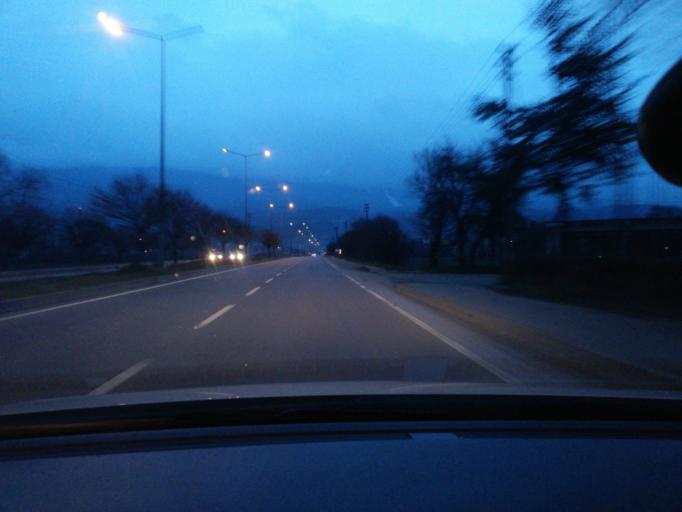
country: TR
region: Bolu
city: Bolu
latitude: 40.6996
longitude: 31.6184
